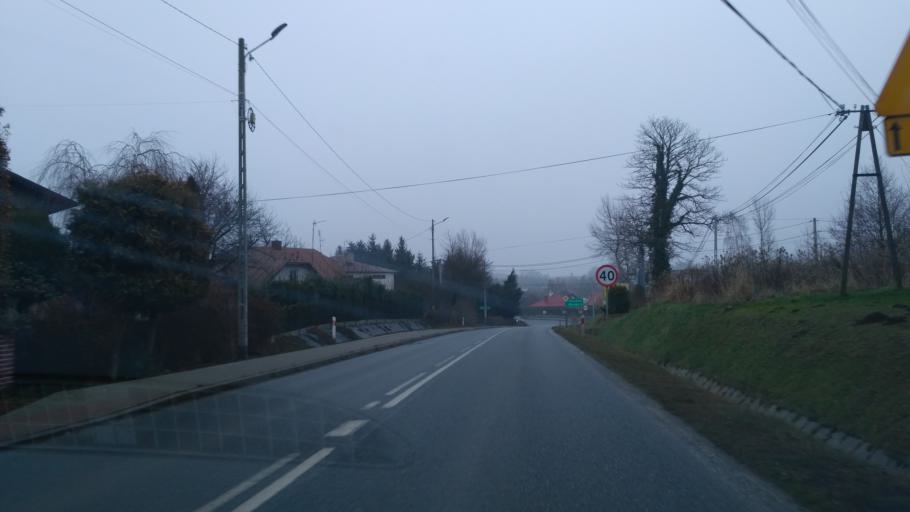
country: PL
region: Subcarpathian Voivodeship
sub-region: Powiat lancucki
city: Sonina
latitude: 50.0569
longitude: 22.2662
